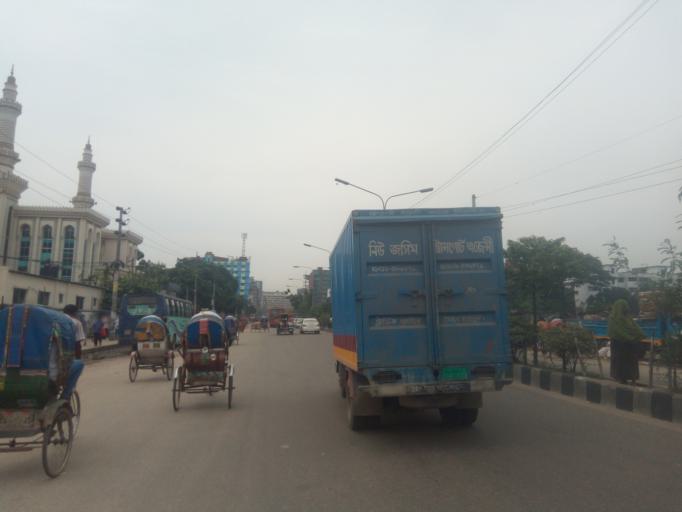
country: BD
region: Dhaka
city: Azimpur
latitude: 23.7922
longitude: 90.3536
